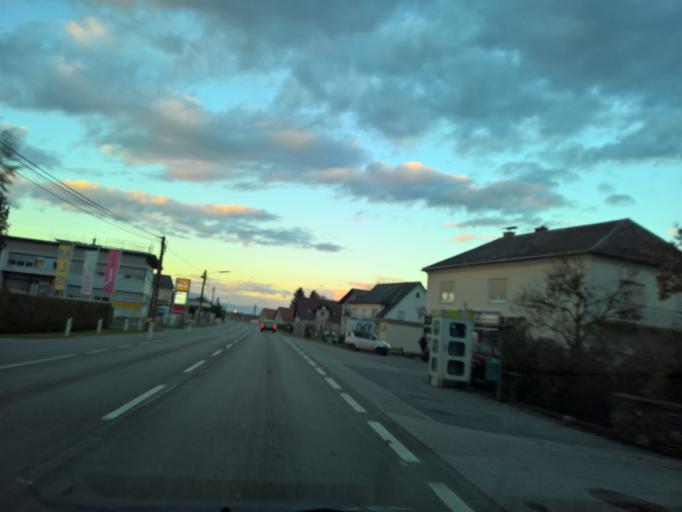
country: AT
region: Styria
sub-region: Politischer Bezirk Graz-Umgebung
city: Kalsdorf bei Graz
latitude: 46.9476
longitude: 15.4843
